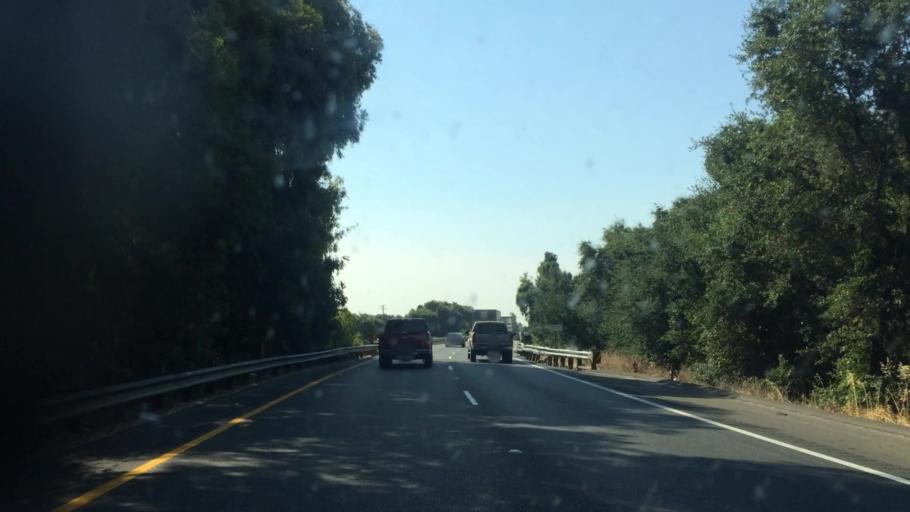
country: US
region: California
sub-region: Sacramento County
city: Elk Grove
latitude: 38.3592
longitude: -121.3446
